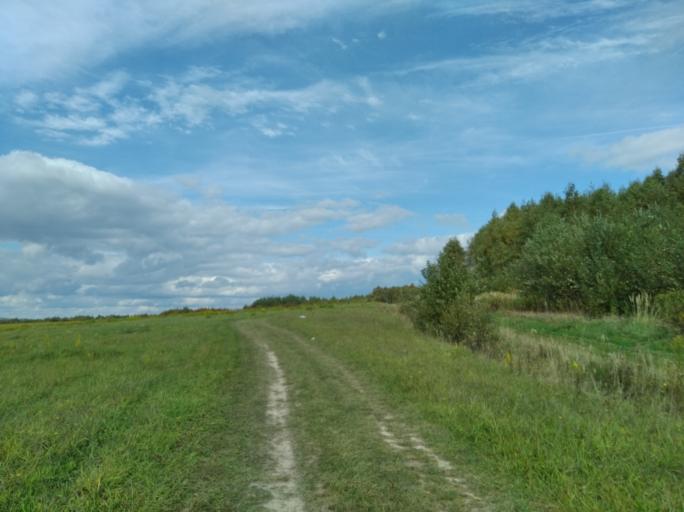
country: PL
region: Subcarpathian Voivodeship
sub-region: Powiat strzyzowski
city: Jawornik
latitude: 49.8328
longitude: 21.9083
